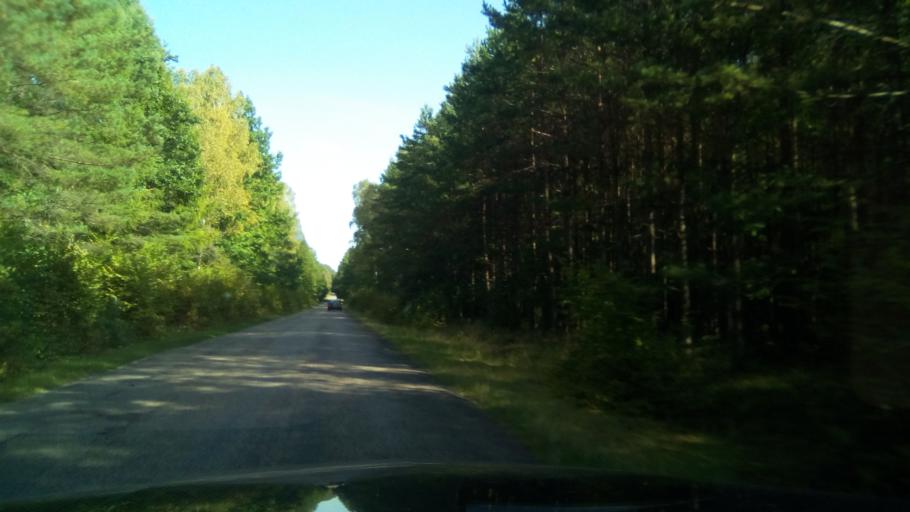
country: PL
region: Greater Poland Voivodeship
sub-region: Powiat zlotowski
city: Sypniewo
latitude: 53.4217
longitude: 16.5942
